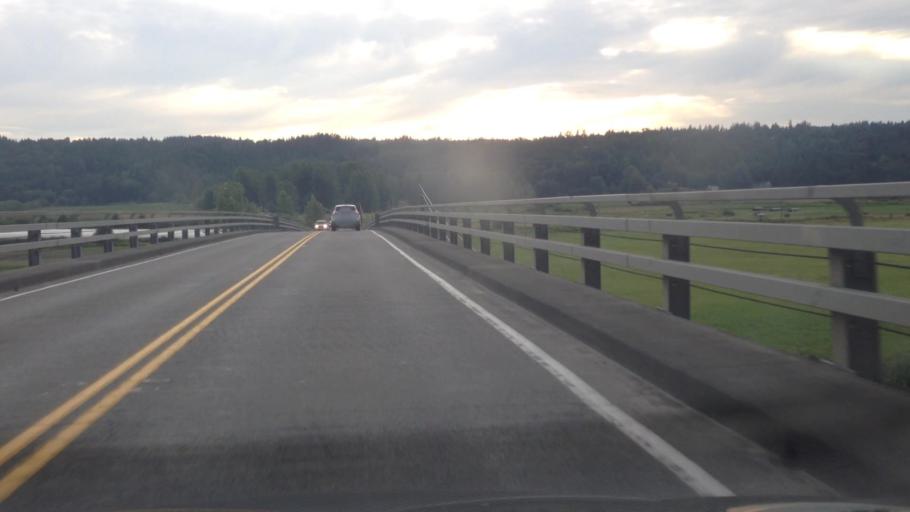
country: US
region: Washington
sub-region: King County
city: Duvall
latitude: 47.7433
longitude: -121.9881
